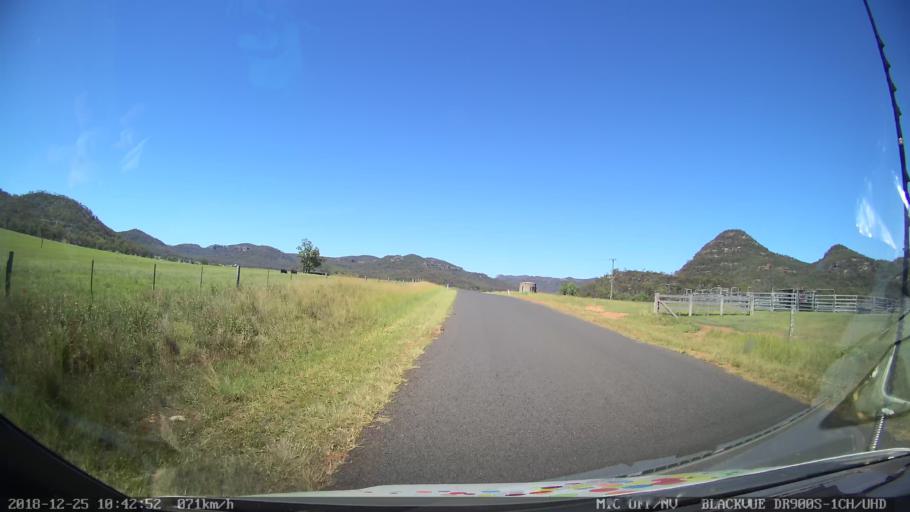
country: AU
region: New South Wales
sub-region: Upper Hunter Shire
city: Merriwa
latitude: -32.4184
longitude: 150.3188
